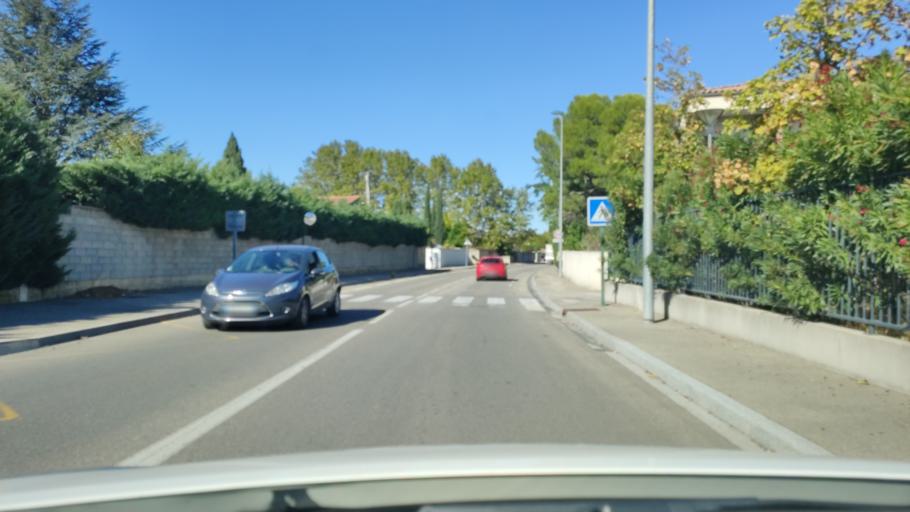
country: FR
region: Provence-Alpes-Cote d'Azur
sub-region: Departement du Vaucluse
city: Morieres-les-Avignon
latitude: 43.9373
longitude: 4.9022
